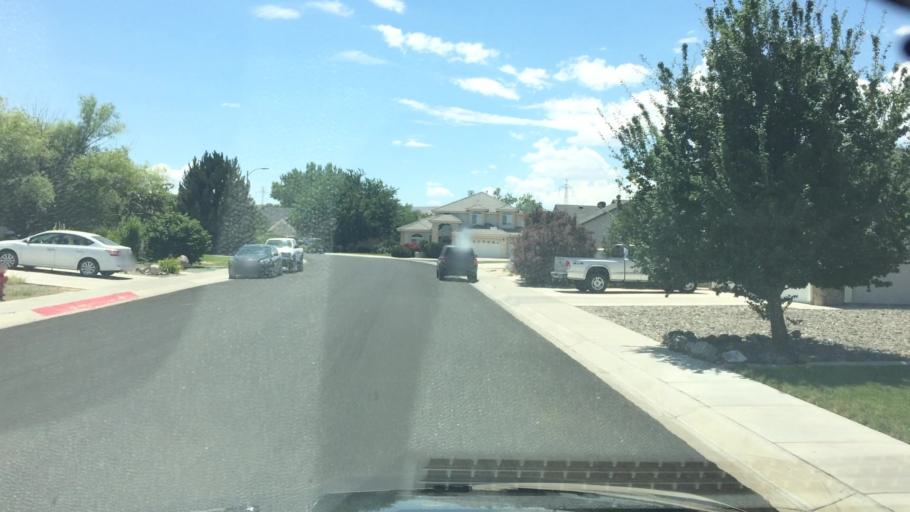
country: US
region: Nevada
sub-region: Lyon County
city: Fernley
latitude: 39.5874
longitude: -119.1522
